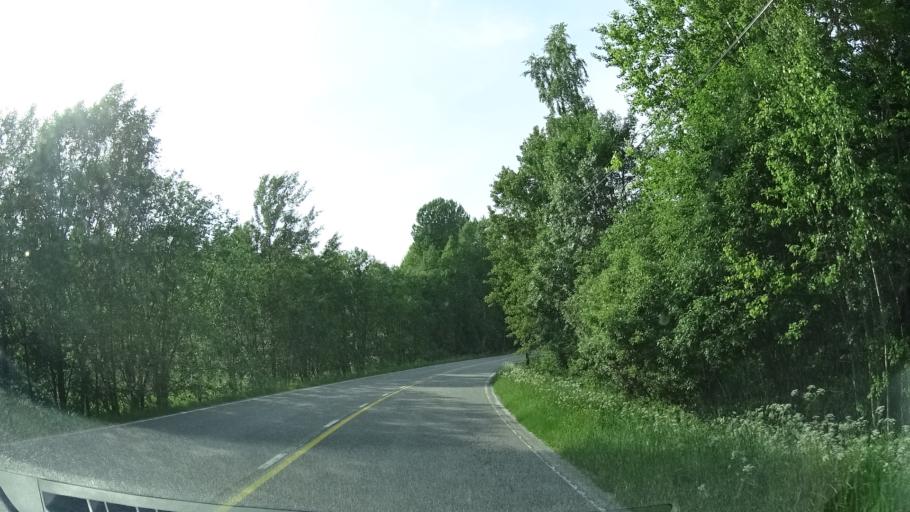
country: FI
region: Uusimaa
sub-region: Helsinki
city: Kirkkonummi
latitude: 60.1047
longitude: 24.4804
